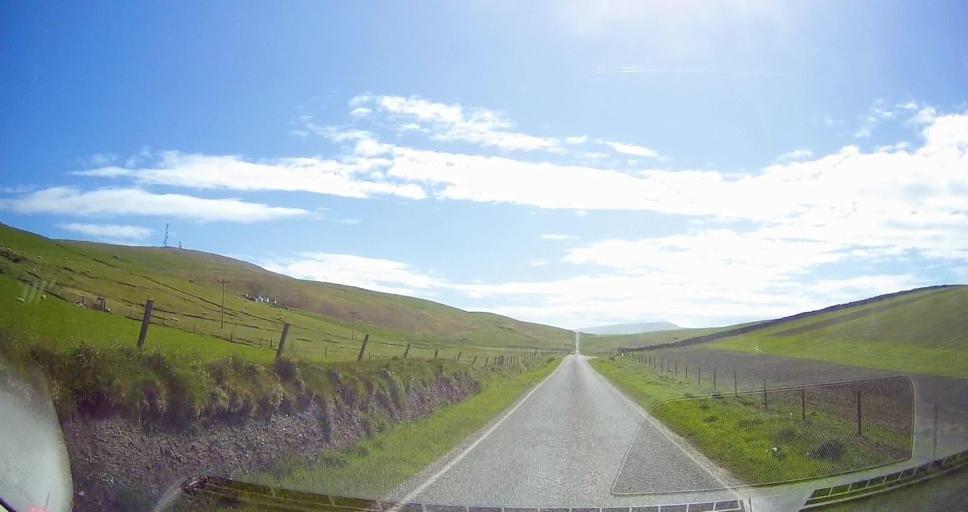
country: GB
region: Scotland
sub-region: Shetland Islands
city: Sandwick
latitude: 59.9684
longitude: -1.3187
